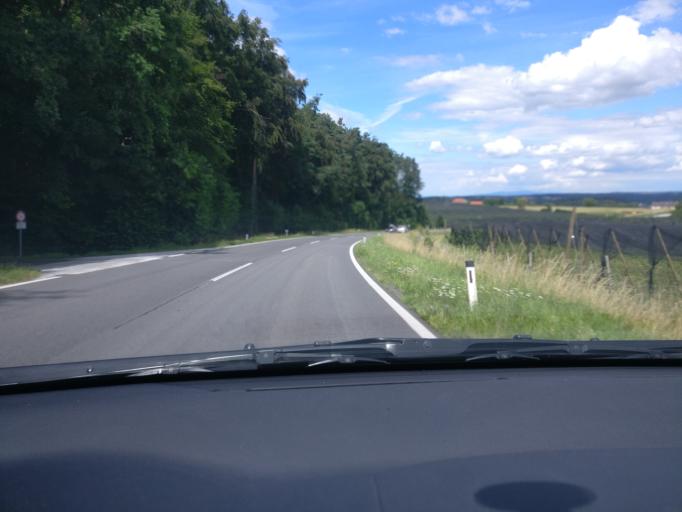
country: AT
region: Styria
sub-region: Politischer Bezirk Hartberg-Fuerstenfeld
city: Kaibing
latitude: 47.2130
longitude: 15.8563
